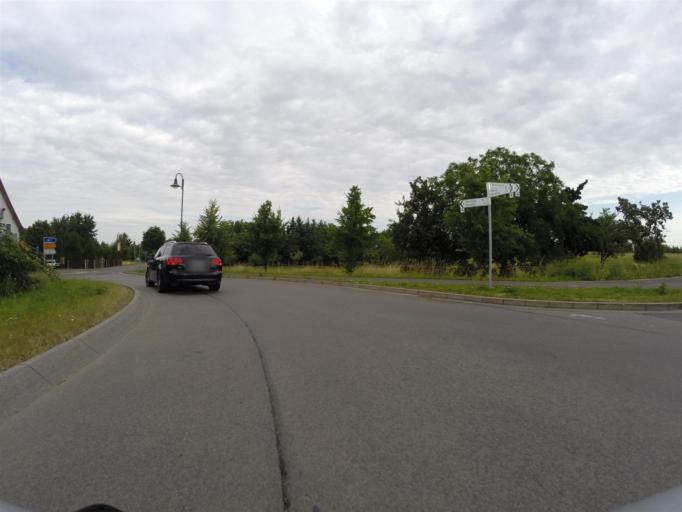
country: DE
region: Thuringia
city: Berlstedt
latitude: 51.0629
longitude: 11.2475
